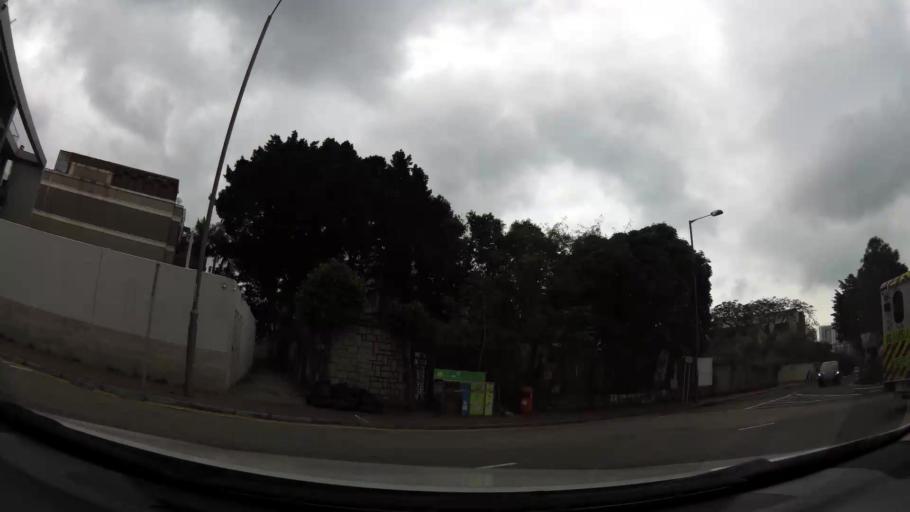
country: HK
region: Wong Tai Sin
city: Wong Tai Sin
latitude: 22.3340
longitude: 114.1815
